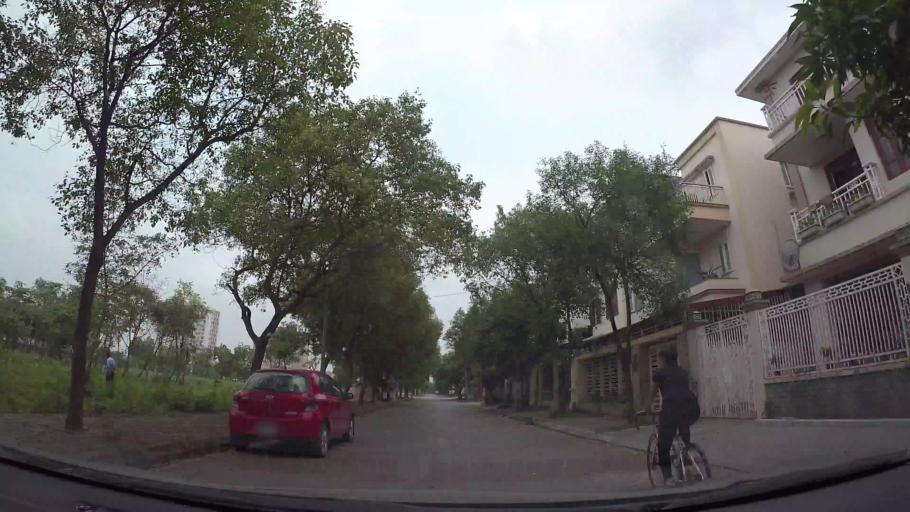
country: VN
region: Ha Noi
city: Trau Quy
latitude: 21.0592
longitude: 105.9106
